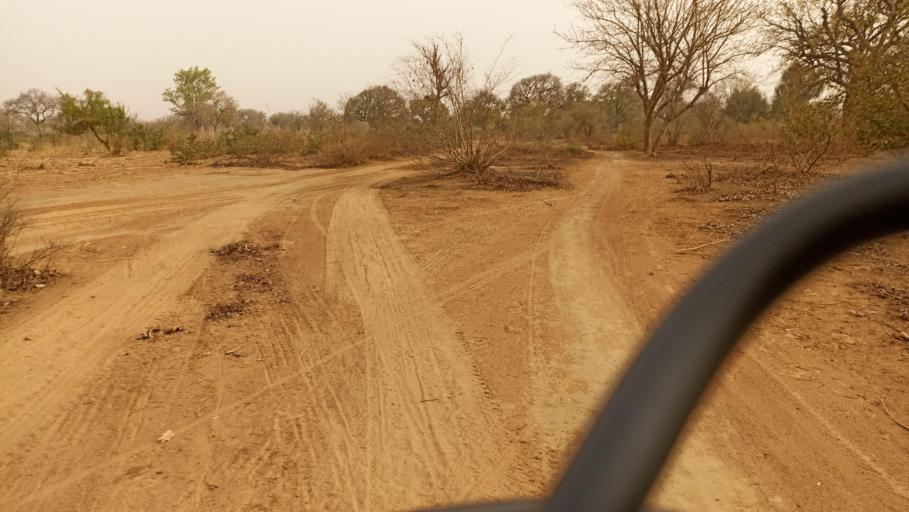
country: BF
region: Nord
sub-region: Province du Zondoma
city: Gourcy
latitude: 13.1611
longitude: -2.5933
